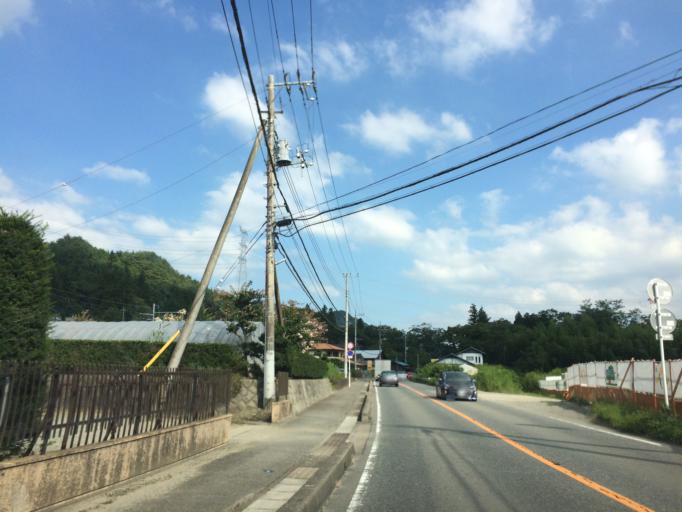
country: JP
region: Gunma
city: Nakanojomachi
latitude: 36.5669
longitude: 138.7490
